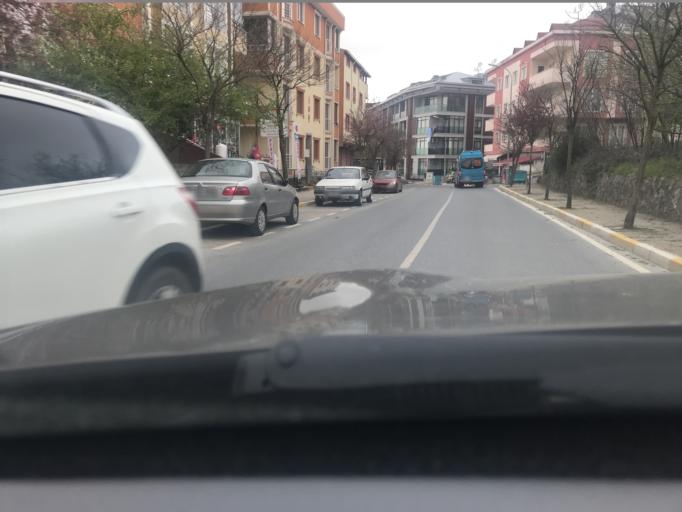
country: TR
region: Istanbul
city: Umraniye
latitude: 41.0356
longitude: 29.1654
